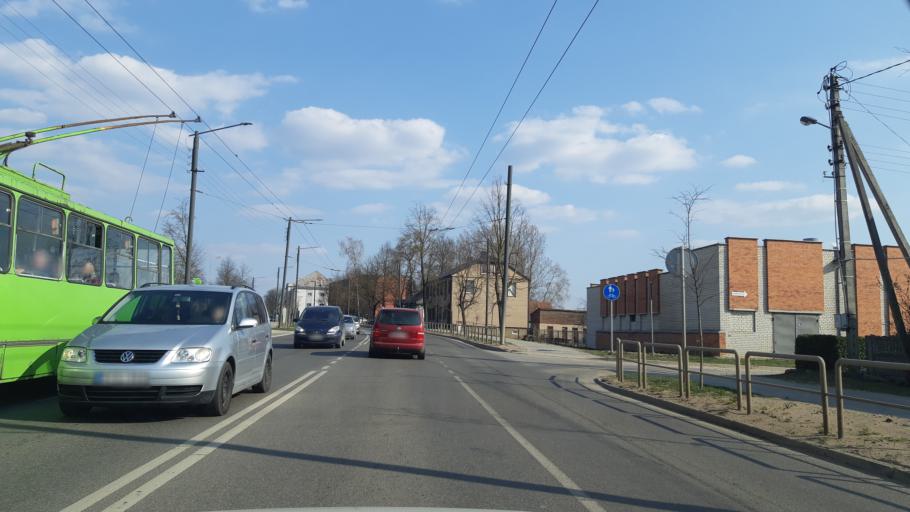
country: LT
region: Kauno apskritis
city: Dainava (Kaunas)
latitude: 54.8952
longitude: 23.9835
